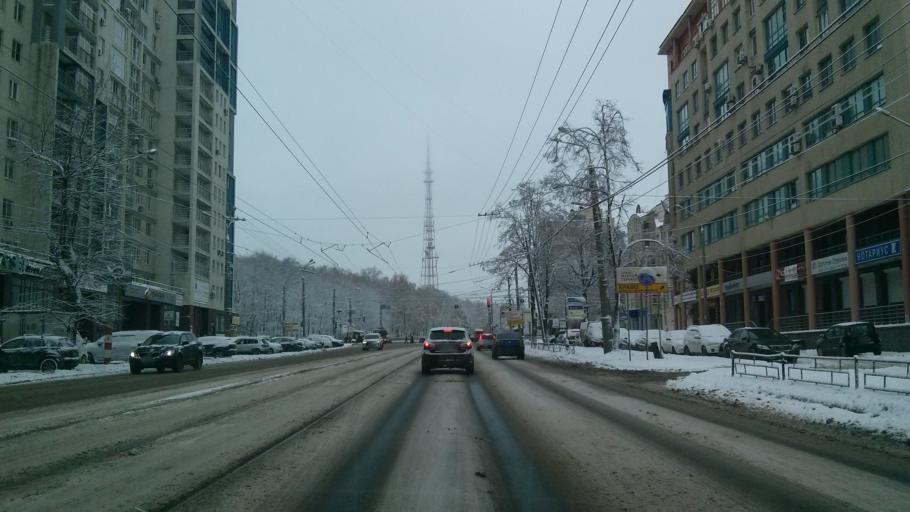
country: RU
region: Nizjnij Novgorod
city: Nizhniy Novgorod
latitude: 56.3112
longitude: 44.0016
